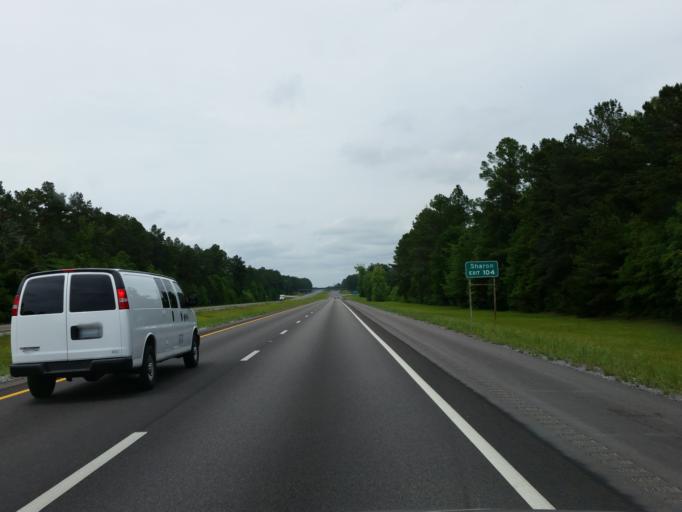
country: US
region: Mississippi
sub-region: Jones County
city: Sharon
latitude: 31.7756
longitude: -89.0564
